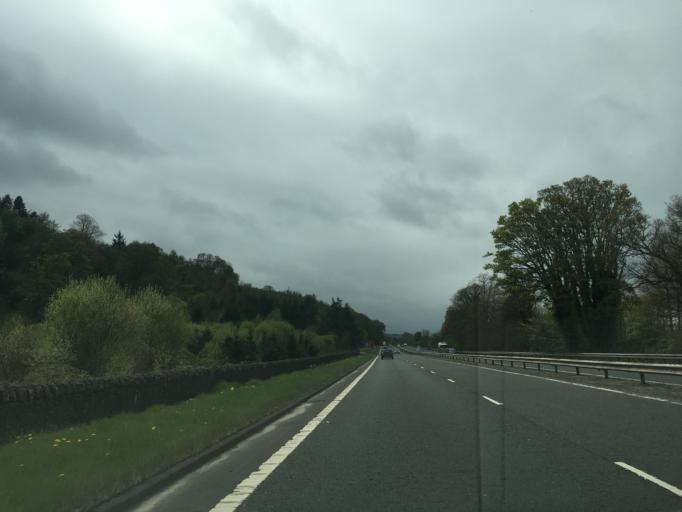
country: GB
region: Scotland
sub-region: Inverclyde
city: Kilmacolm
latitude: 55.9304
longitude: -4.6211
